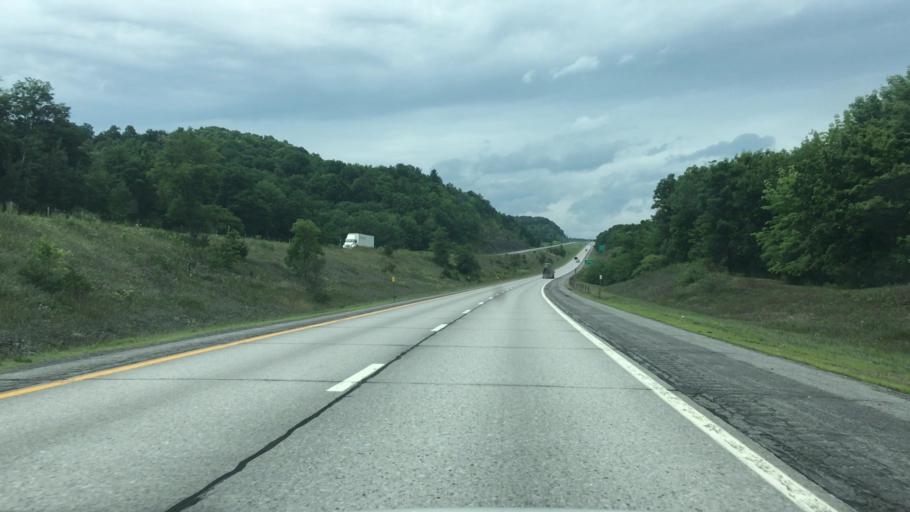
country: US
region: New York
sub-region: Schoharie County
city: Schoharie
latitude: 42.6800
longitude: -74.3822
